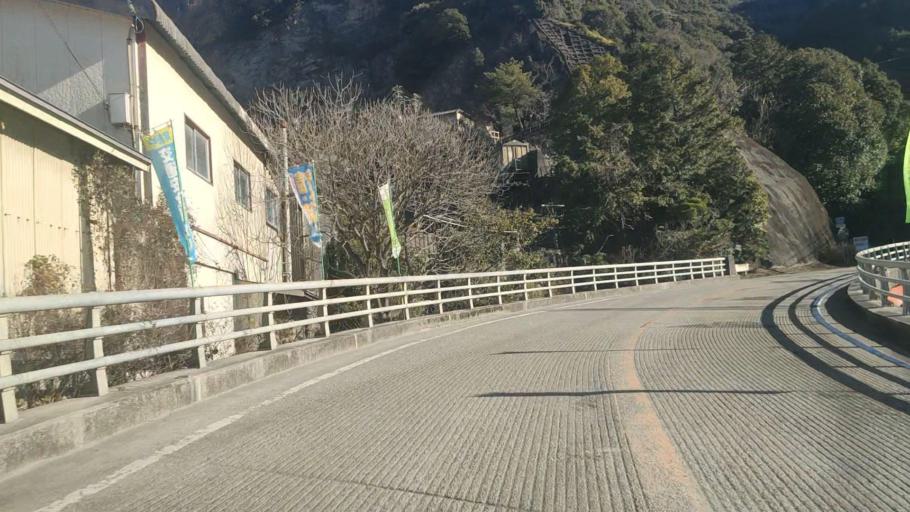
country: JP
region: Miyazaki
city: Nobeoka
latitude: 32.6287
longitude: 131.7176
